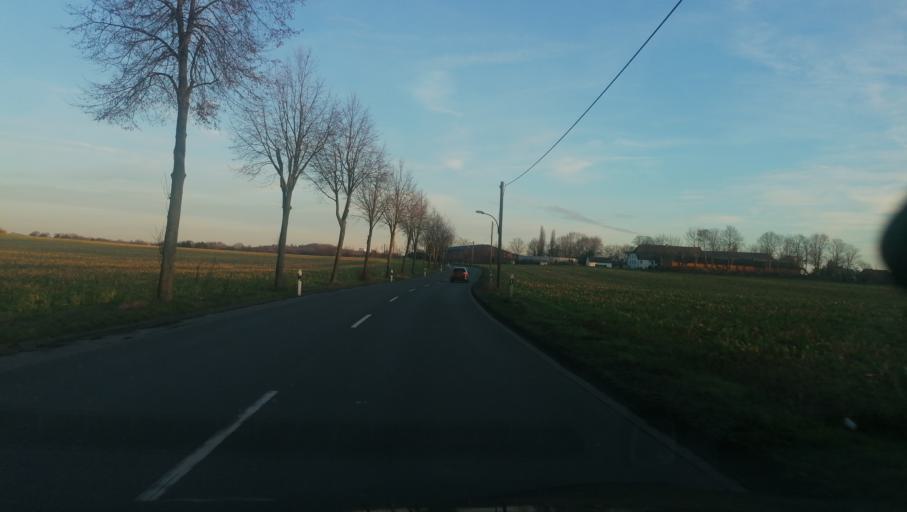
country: DE
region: North Rhine-Westphalia
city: Bergkamen
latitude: 51.5962
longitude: 7.6147
